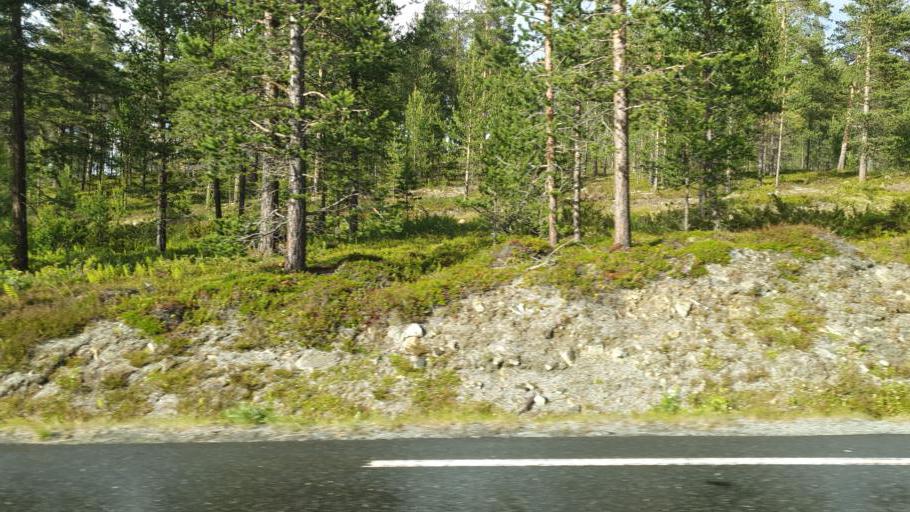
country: NO
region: Oppland
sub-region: Vaga
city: Vagamo
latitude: 61.8177
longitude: 8.9829
